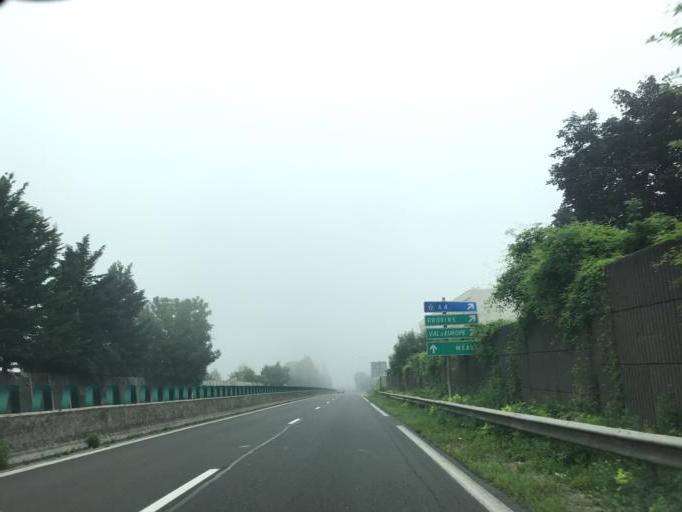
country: FR
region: Ile-de-France
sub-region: Departement de Seine-et-Marne
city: Lagny-sur-Marne
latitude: 48.8734
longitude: 2.7180
